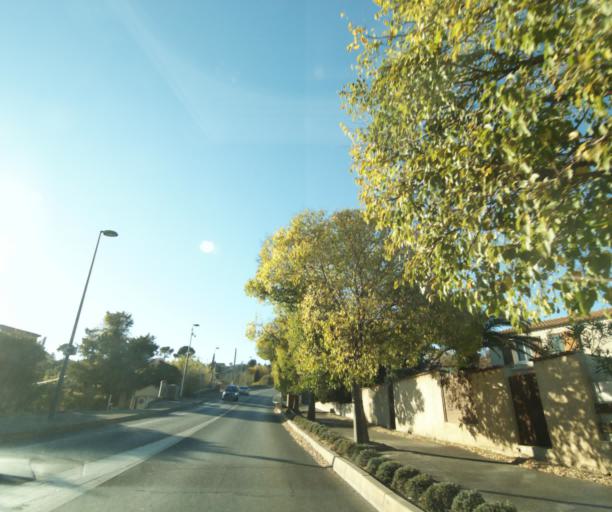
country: FR
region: Provence-Alpes-Cote d'Azur
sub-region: Departement des Bouches-du-Rhone
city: Plan-de-Cuques
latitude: 43.3465
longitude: 5.4561
